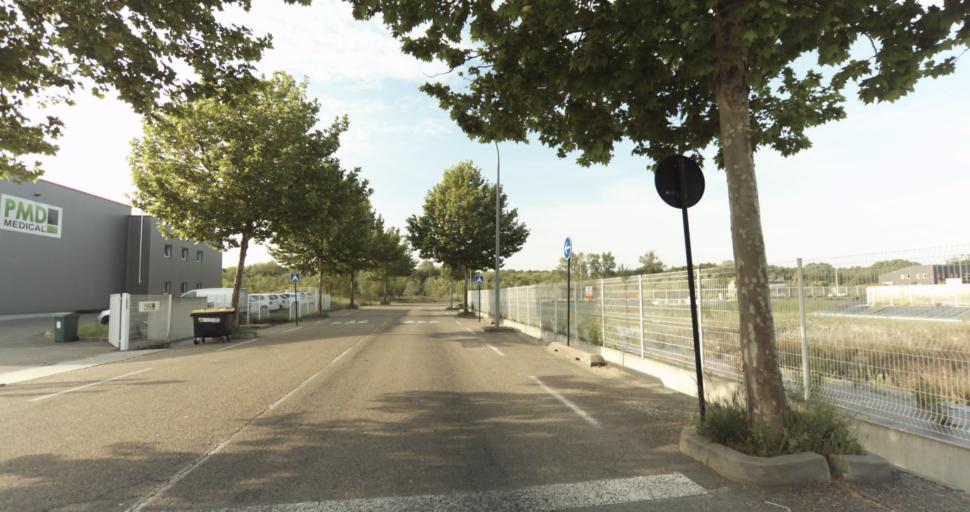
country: FR
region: Languedoc-Roussillon
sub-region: Departement du Gard
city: Rodilhan
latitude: 43.8376
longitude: 4.4291
